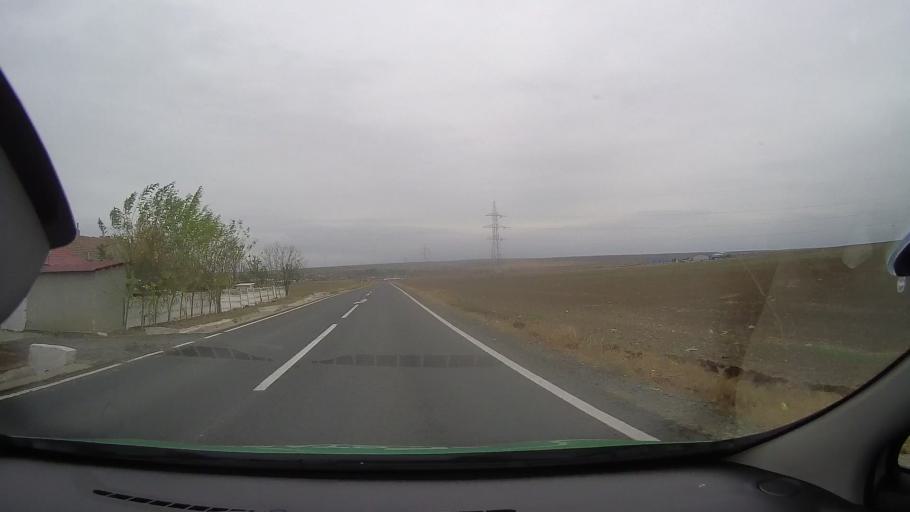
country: RO
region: Constanta
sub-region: Comuna Nicolae Balcescu
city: Dorobantu
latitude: 44.4191
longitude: 28.3134
